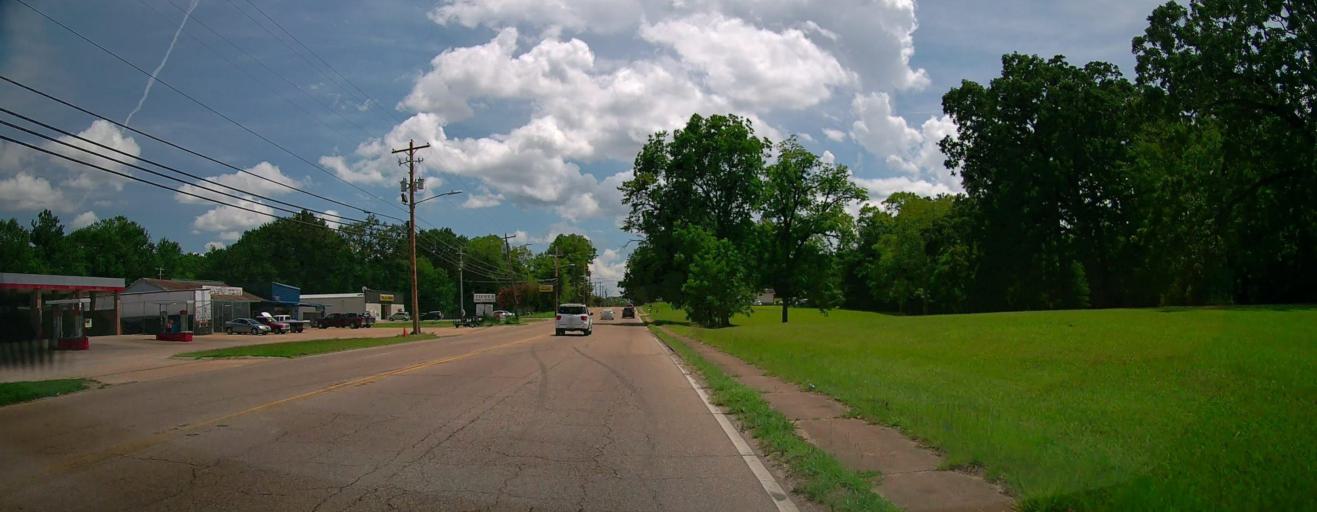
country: US
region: Mississippi
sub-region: Lee County
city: Verona
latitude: 34.1983
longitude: -88.7201
